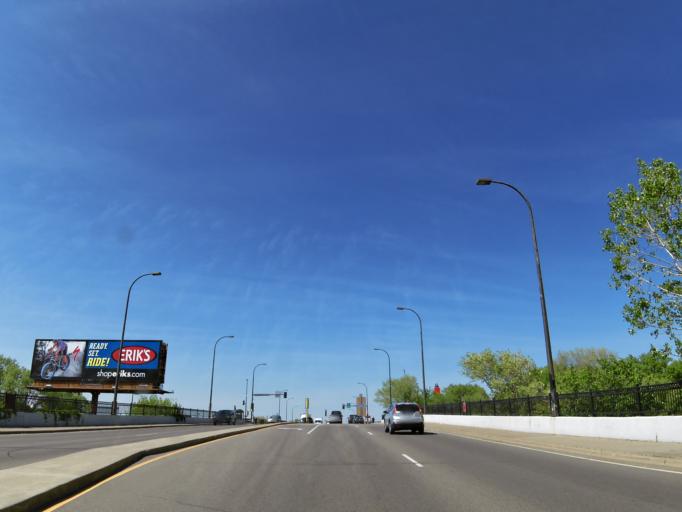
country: US
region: Minnesota
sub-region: Hennepin County
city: Minneapolis
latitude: 44.9976
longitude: -93.2472
